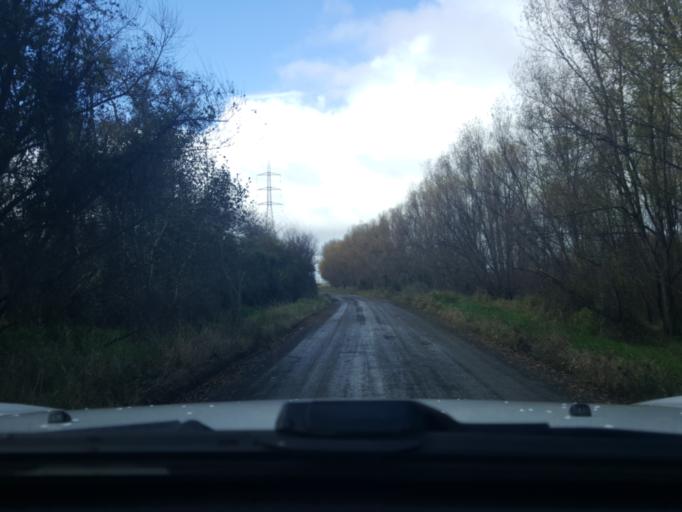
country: NZ
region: Waikato
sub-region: Waikato District
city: Te Kauwhata
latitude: -37.4116
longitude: 175.0602
